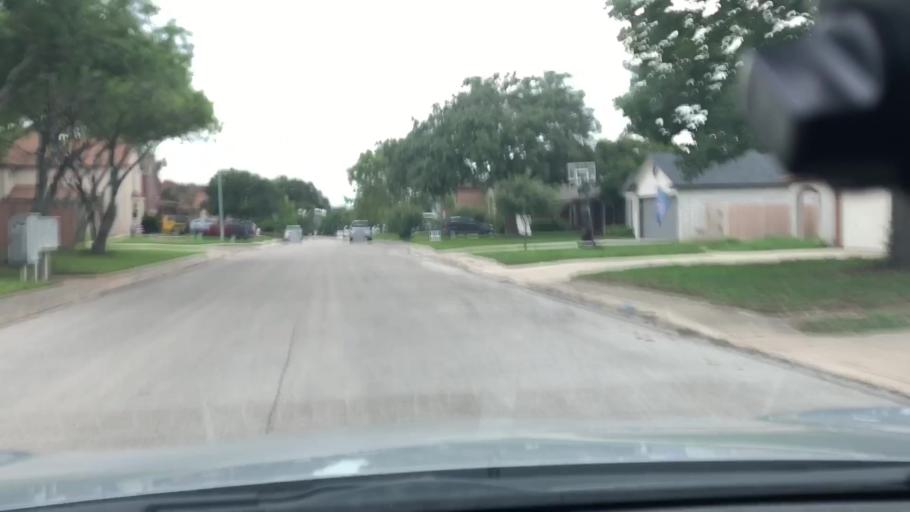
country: US
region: Texas
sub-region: Bexar County
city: Leon Valley
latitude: 29.5056
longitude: -98.6770
